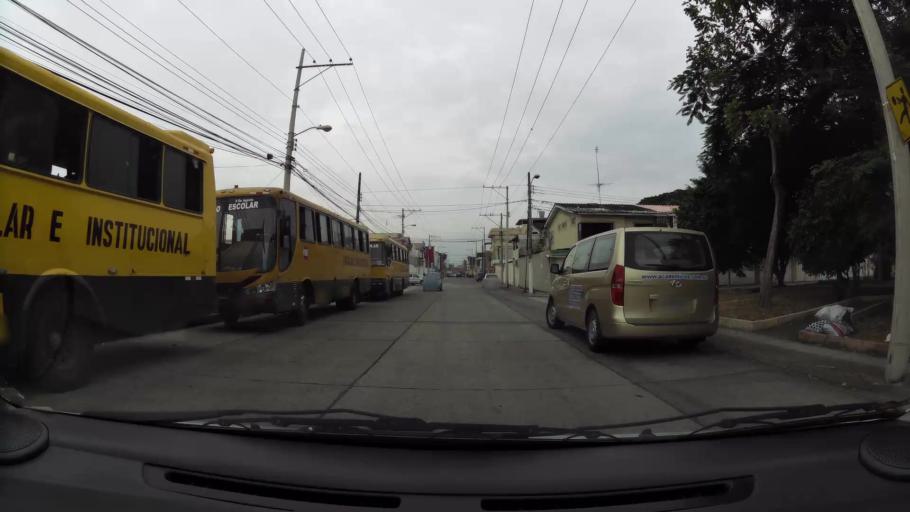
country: EC
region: Guayas
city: Eloy Alfaro
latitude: -2.1426
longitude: -79.8847
